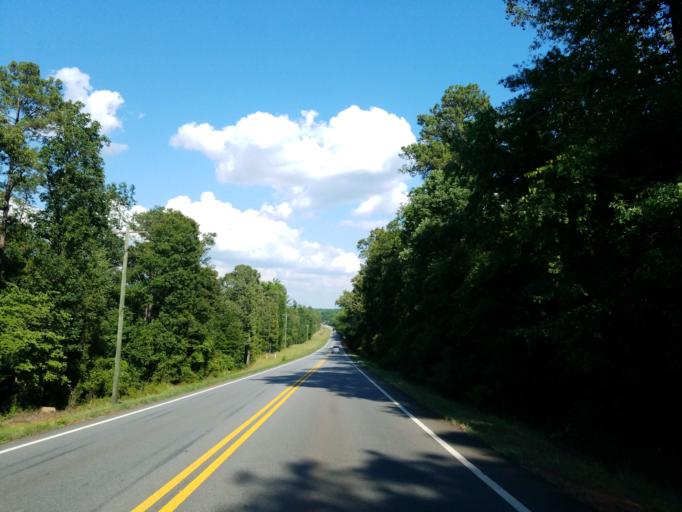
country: US
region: Georgia
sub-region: Houston County
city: Perry
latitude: 32.5517
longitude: -83.7743
